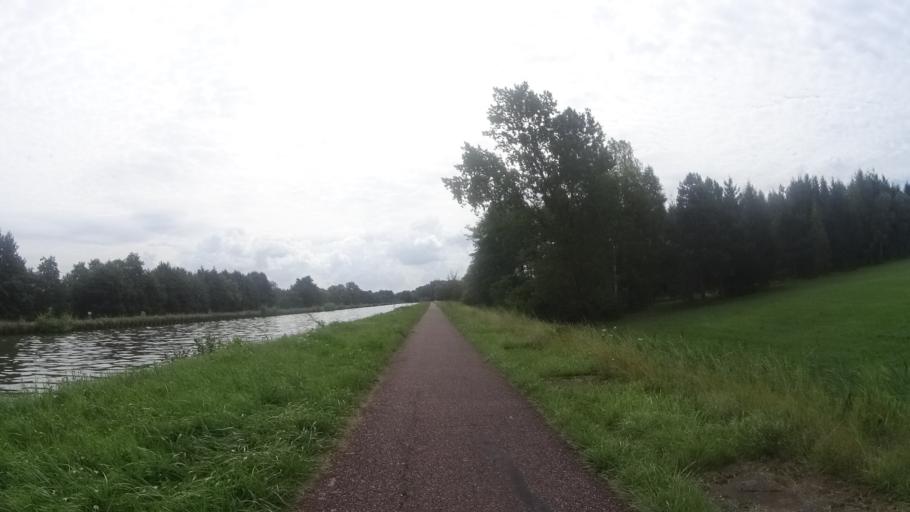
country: FR
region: Alsace
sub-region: Departement du Bas-Rhin
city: Steinbourg
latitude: 48.7610
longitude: 7.4389
